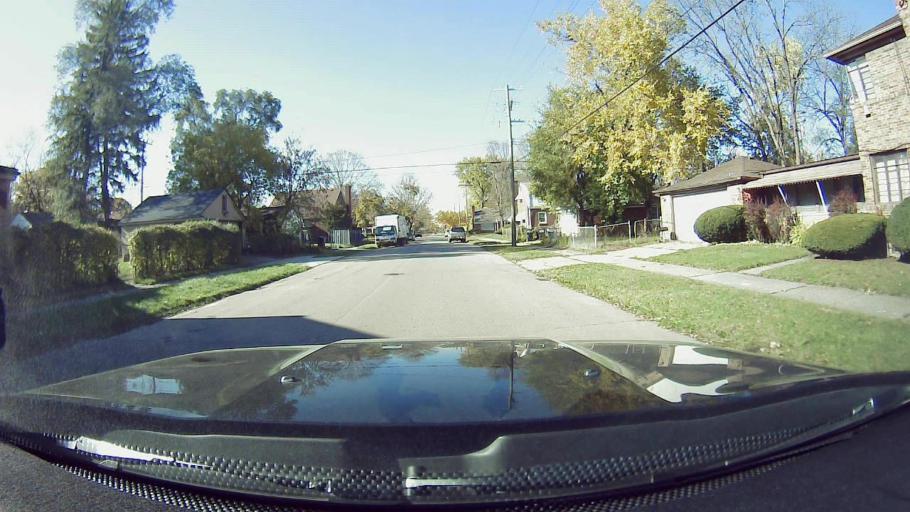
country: US
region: Michigan
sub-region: Wayne County
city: Dearborn Heights
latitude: 42.3890
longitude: -83.2256
